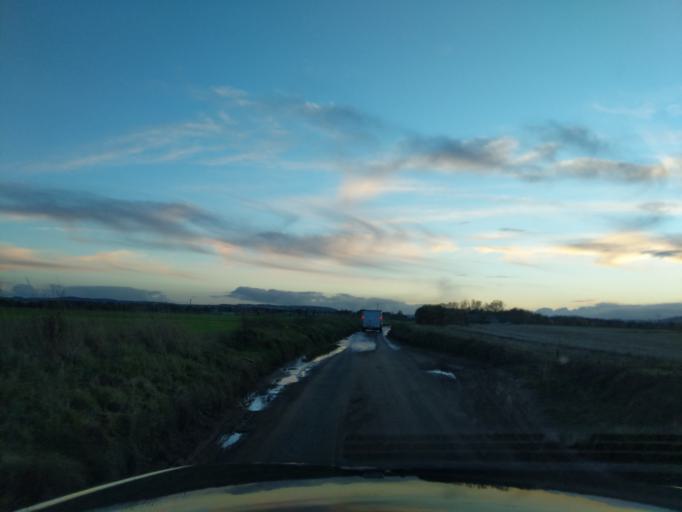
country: GB
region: Scotland
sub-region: Fife
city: Leuchars
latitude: 56.3974
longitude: -2.8652
